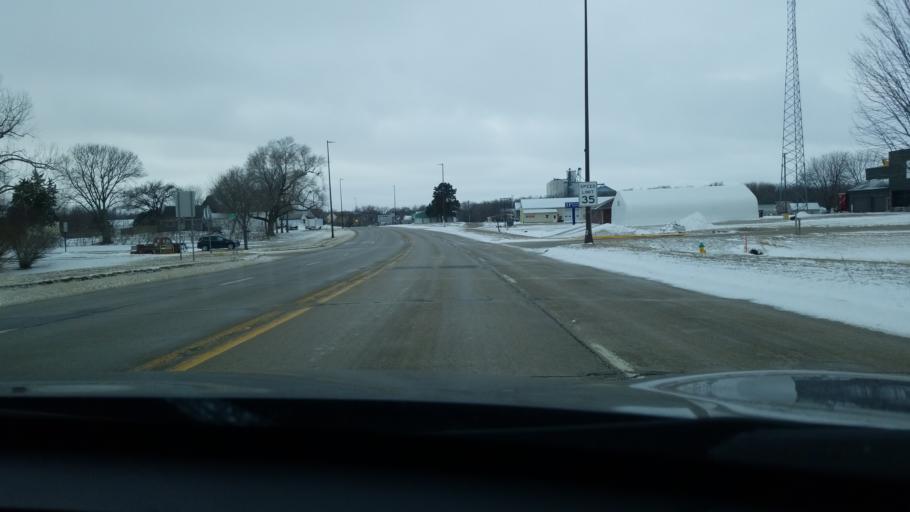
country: US
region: Iowa
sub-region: Lyon County
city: Rock Rapids
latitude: 43.4330
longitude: -96.1587
